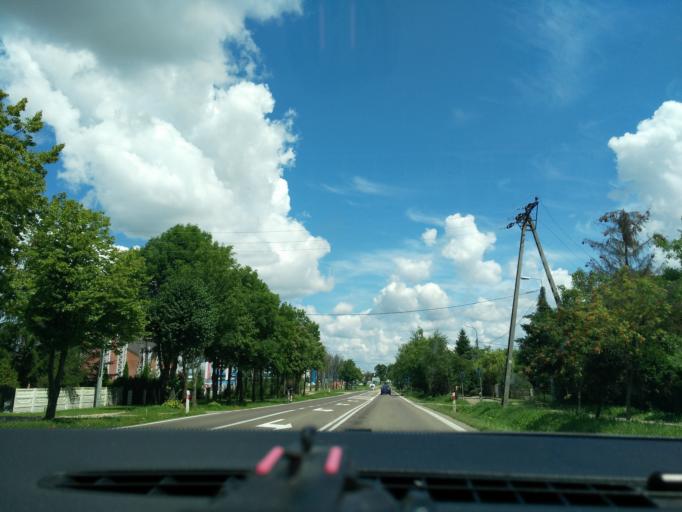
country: PL
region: Podlasie
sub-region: Powiat bielski
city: Bielsk Podlaski
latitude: 52.7527
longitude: 23.1732
